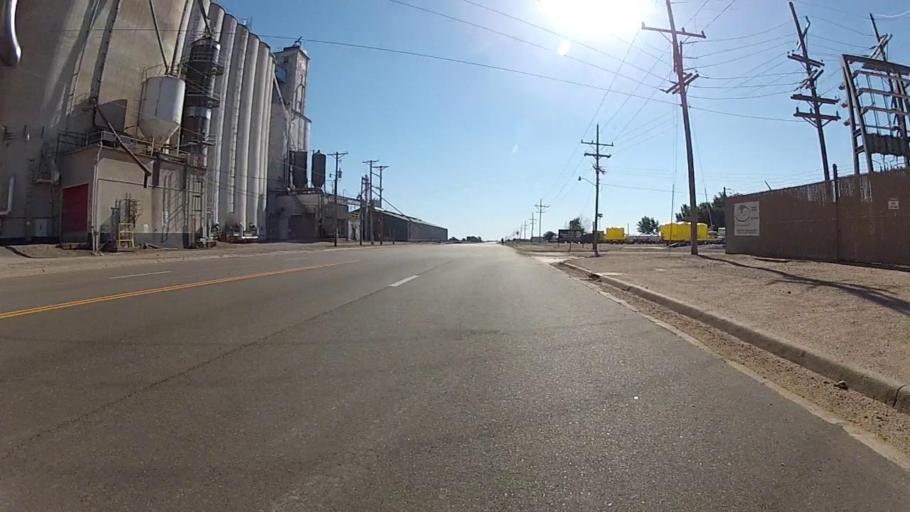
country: US
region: Kansas
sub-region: Haskell County
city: Sublette
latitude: 37.5434
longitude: -100.6272
